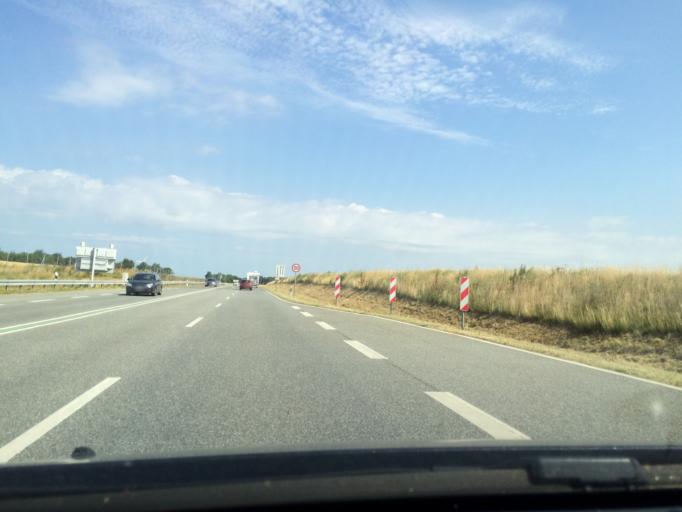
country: DE
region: Mecklenburg-Vorpommern
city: Altefahr
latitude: 54.3315
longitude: 13.1459
